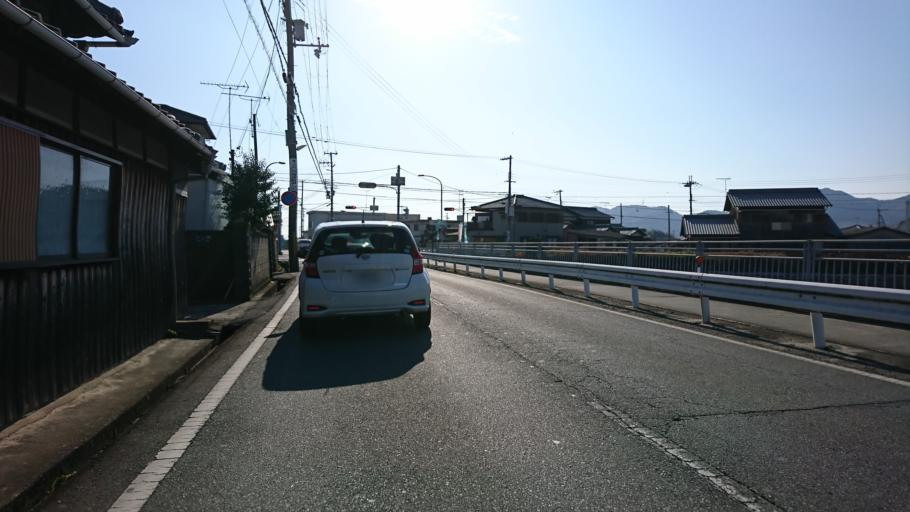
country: JP
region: Hyogo
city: Kakogawacho-honmachi
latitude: 34.8174
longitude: 134.8192
